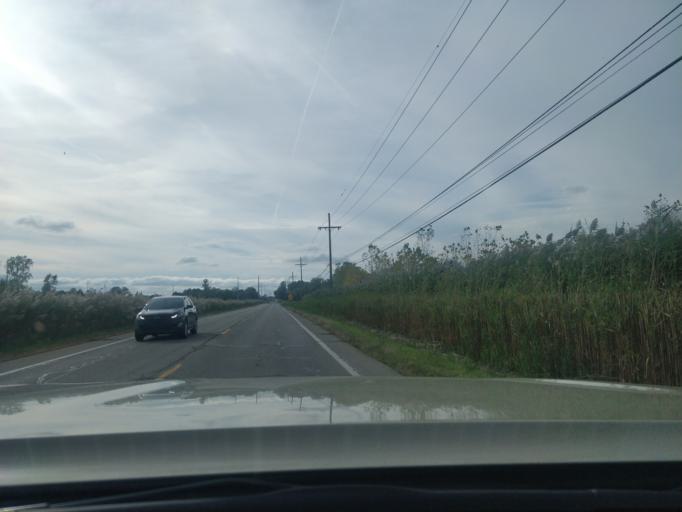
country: US
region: Michigan
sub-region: Wayne County
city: Romulus
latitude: 42.1804
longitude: -83.3670
